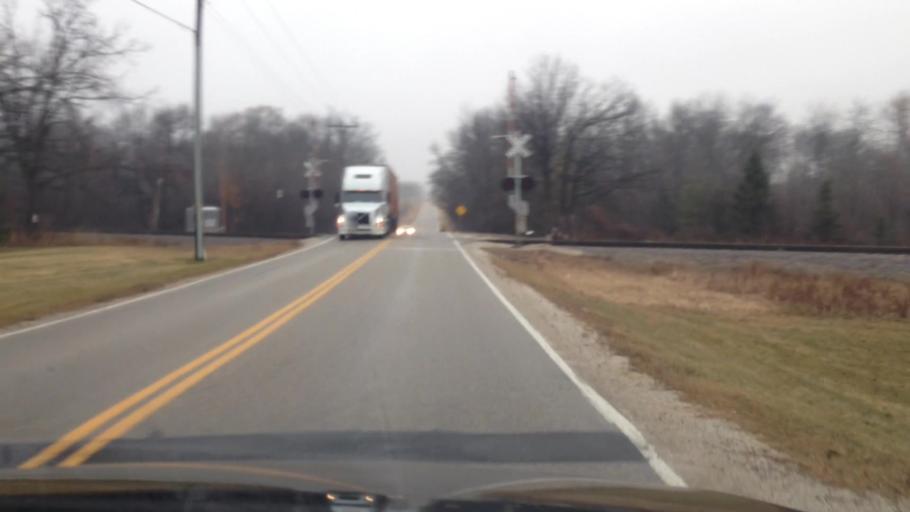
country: US
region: Wisconsin
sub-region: Washington County
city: Germantown
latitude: 43.2375
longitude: -88.1429
